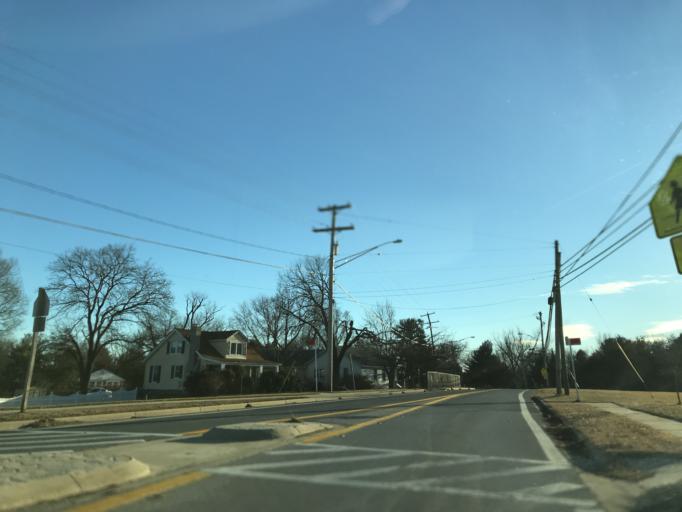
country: US
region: Maryland
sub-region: Montgomery County
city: Burtonsville
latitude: 39.0959
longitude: -76.9460
